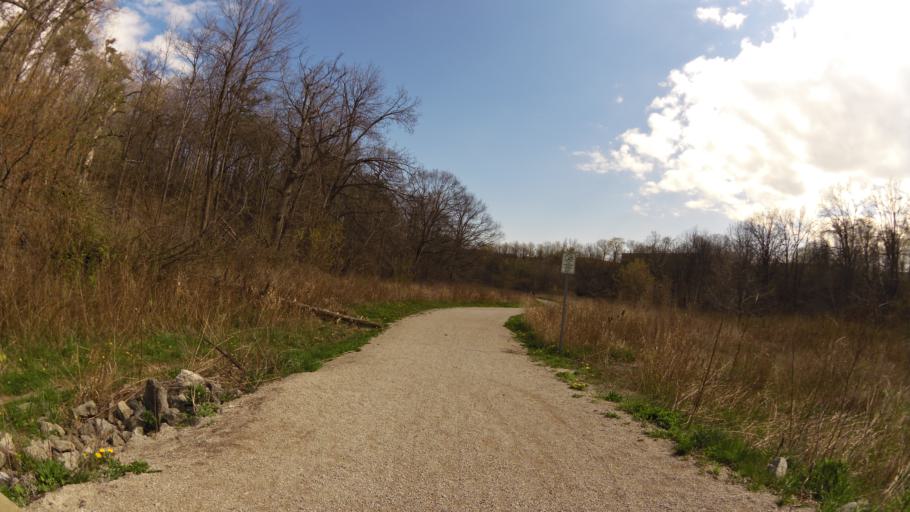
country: CA
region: Ontario
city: Etobicoke
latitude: 43.6488
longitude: -79.6162
